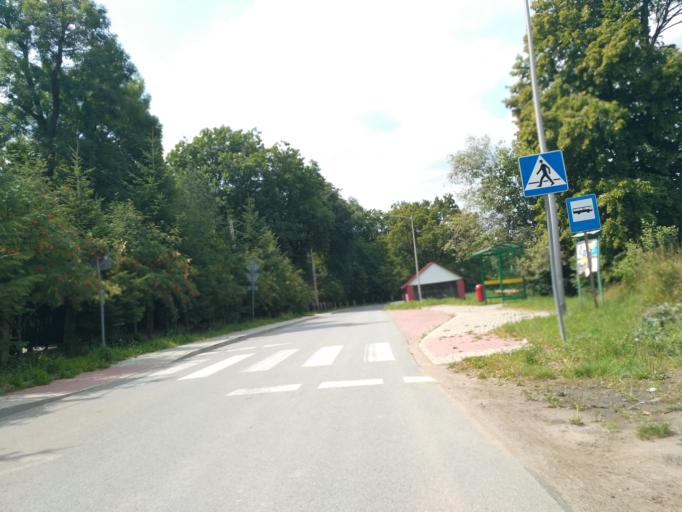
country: PL
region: Subcarpathian Voivodeship
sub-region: Powiat krosnienski
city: Rymanow
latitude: 49.5889
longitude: 21.8302
